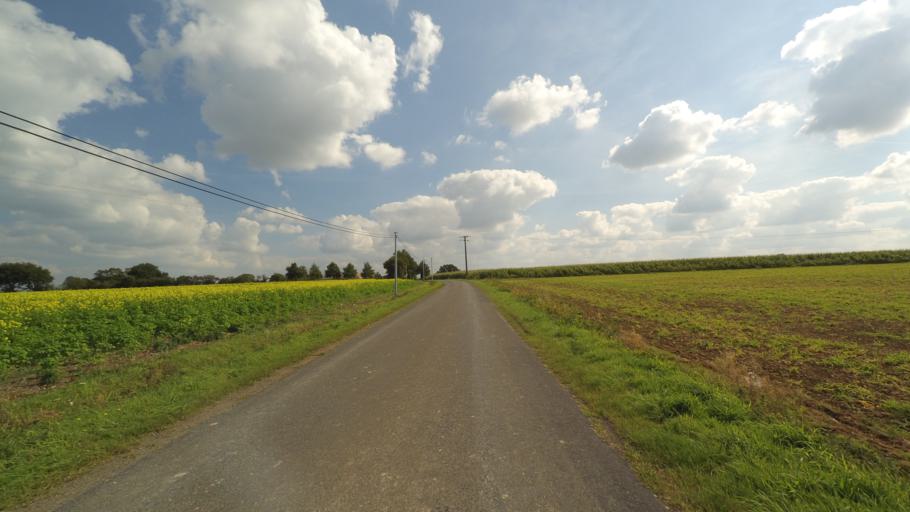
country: FR
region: Pays de la Loire
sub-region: Departement de la Vendee
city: Bouffere
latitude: 46.9559
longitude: -1.3780
